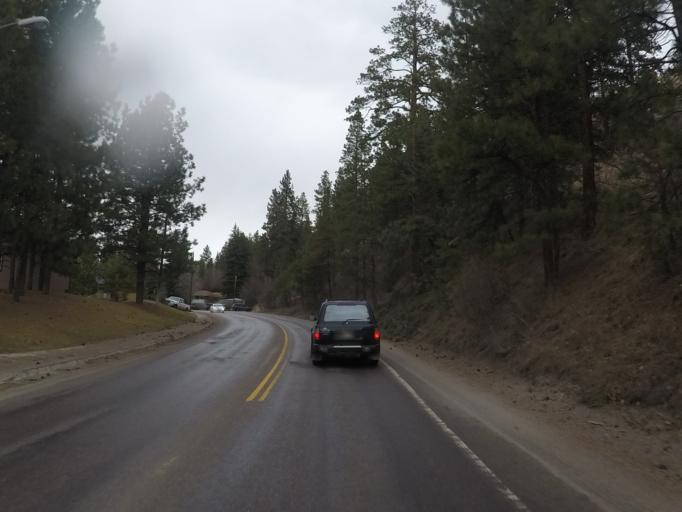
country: US
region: Montana
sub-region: Missoula County
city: Missoula
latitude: 46.8776
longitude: -113.9709
